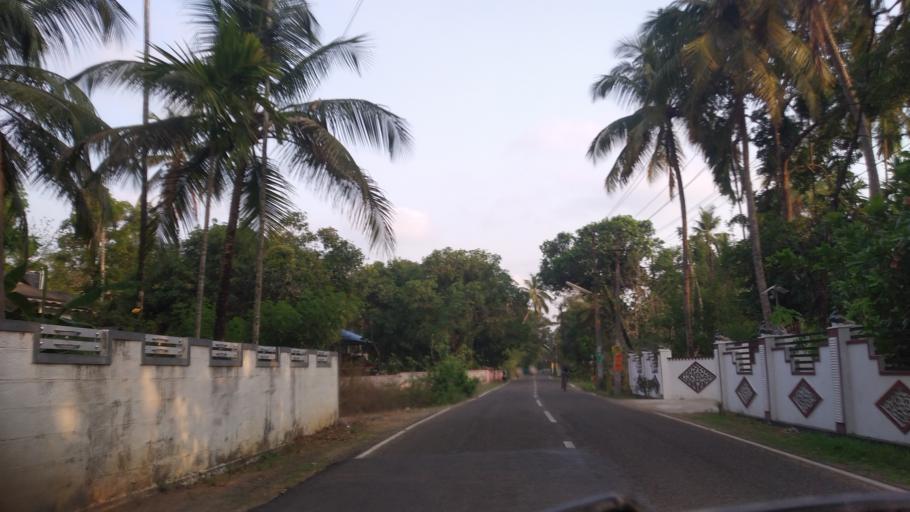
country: IN
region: Kerala
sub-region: Thrissur District
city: Thanniyam
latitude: 10.3641
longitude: 76.1074
